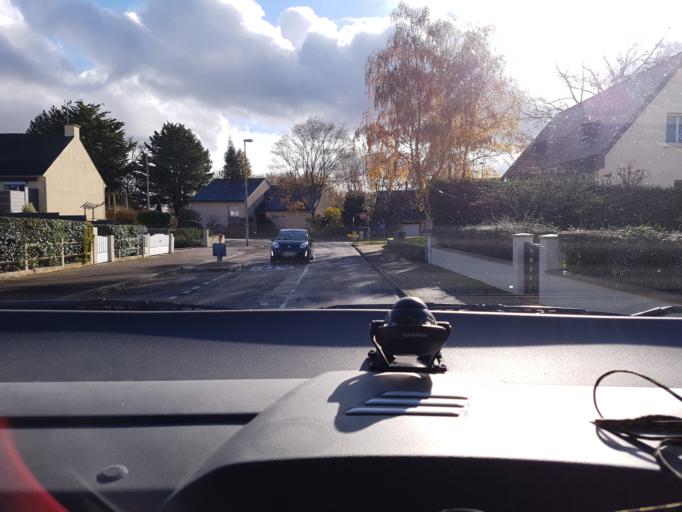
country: FR
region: Brittany
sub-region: Departement d'Ille-et-Vilaine
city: Acigne
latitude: 48.1311
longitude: -1.5441
